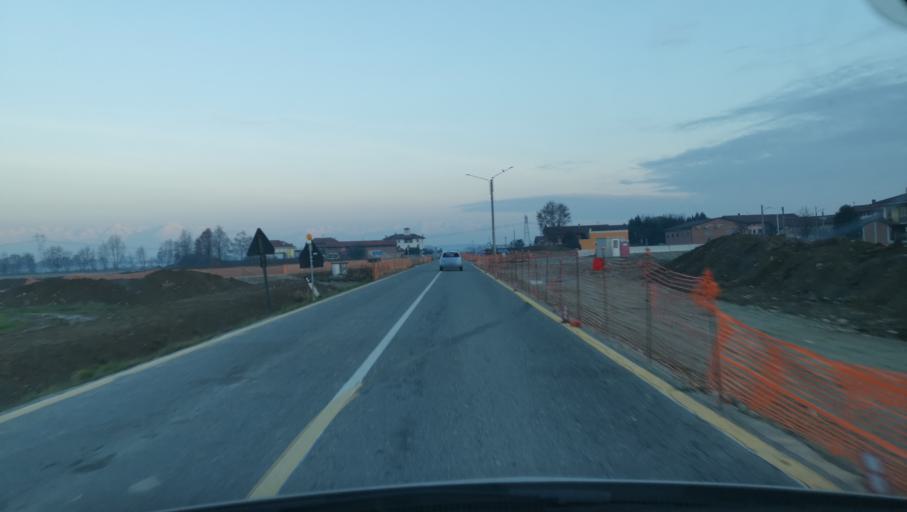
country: IT
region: Piedmont
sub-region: Provincia di Torino
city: Montanaro
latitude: 45.2531
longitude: 7.8918
